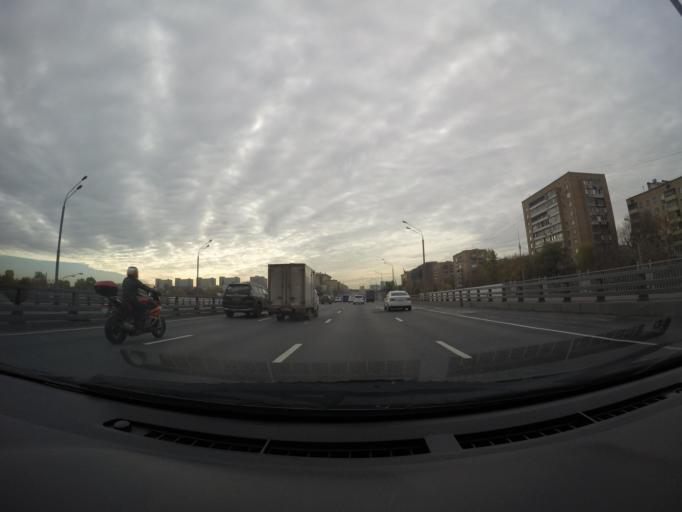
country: RU
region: Moscow
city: Rostokino
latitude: 55.8335
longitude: 37.6543
